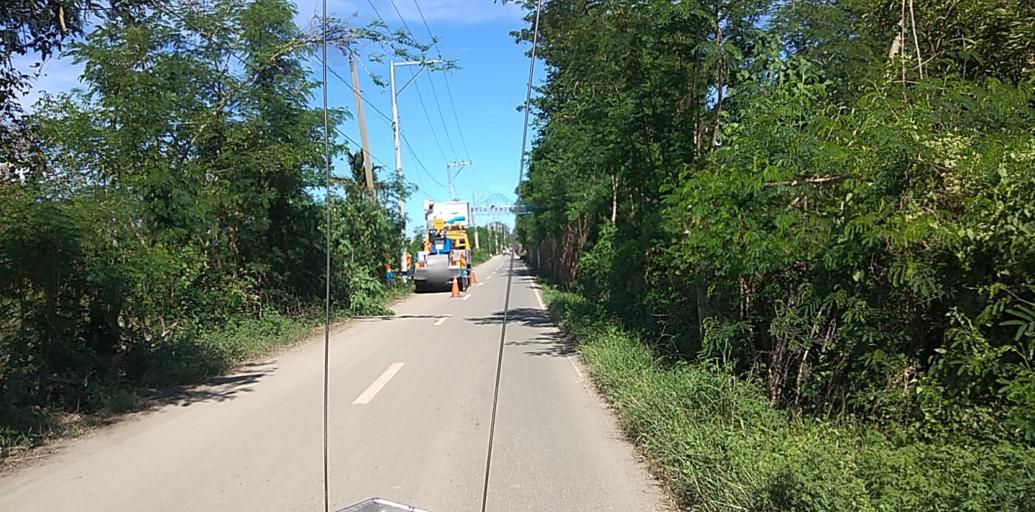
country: PH
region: Central Luzon
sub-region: Province of Pampanga
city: Candaba
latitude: 15.1181
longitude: 120.8141
